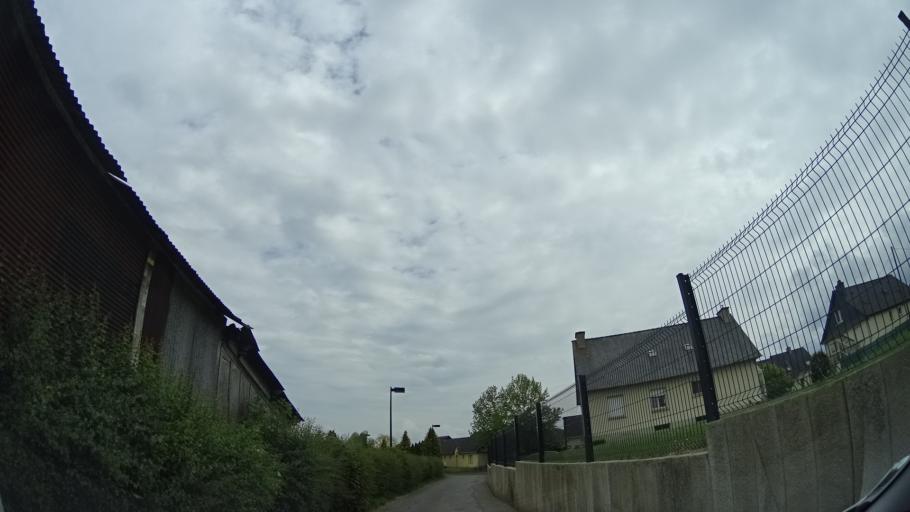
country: FR
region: Brittany
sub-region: Departement d'Ille-et-Vilaine
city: Tinteniac
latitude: 48.3274
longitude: -1.8377
